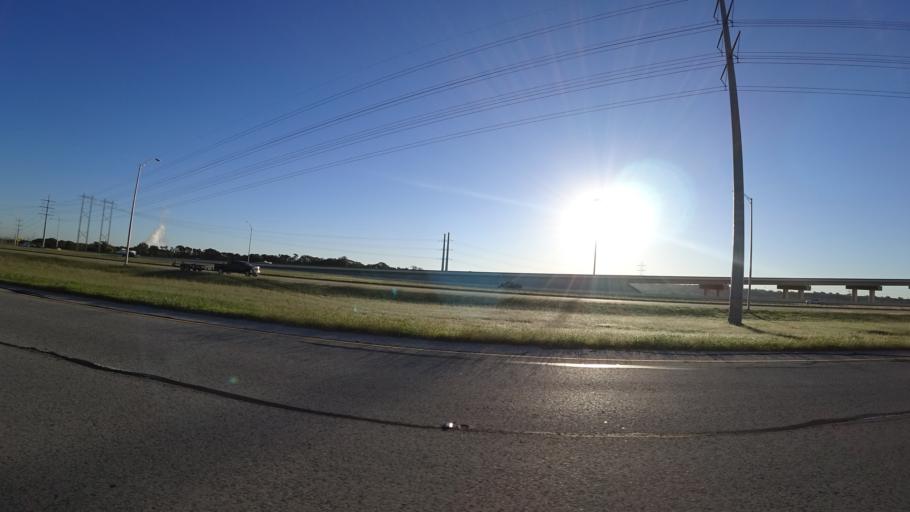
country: US
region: Texas
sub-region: Travis County
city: Hornsby Bend
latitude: 30.2008
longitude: -97.6232
